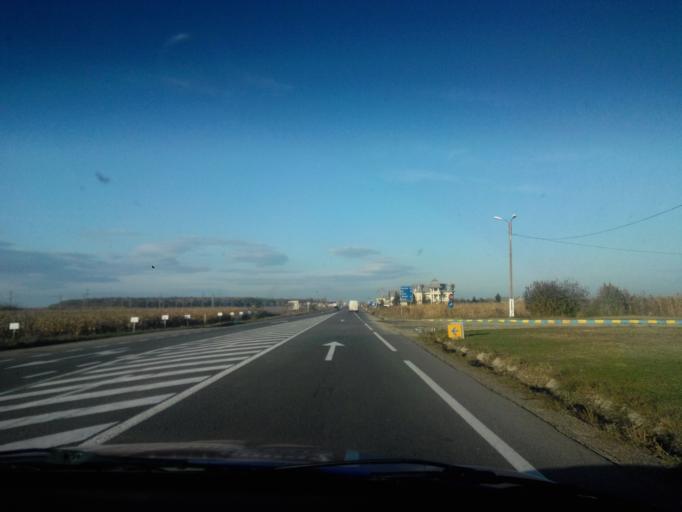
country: RO
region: Neamt
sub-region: Comuna Secueni
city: Secueni
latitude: 46.8576
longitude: 26.8881
